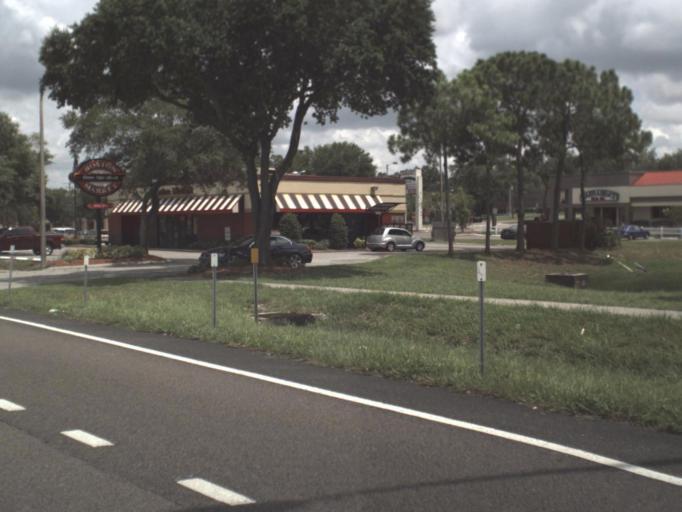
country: US
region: Florida
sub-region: Hillsborough County
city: Temple Terrace
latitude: 28.0543
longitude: -82.3949
